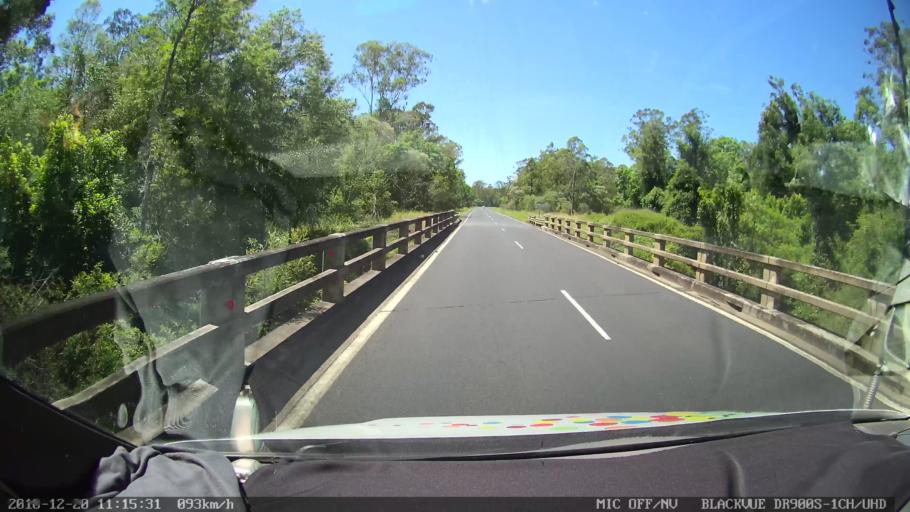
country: AU
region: New South Wales
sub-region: Richmond Valley
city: Casino
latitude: -29.0142
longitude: 153.0092
